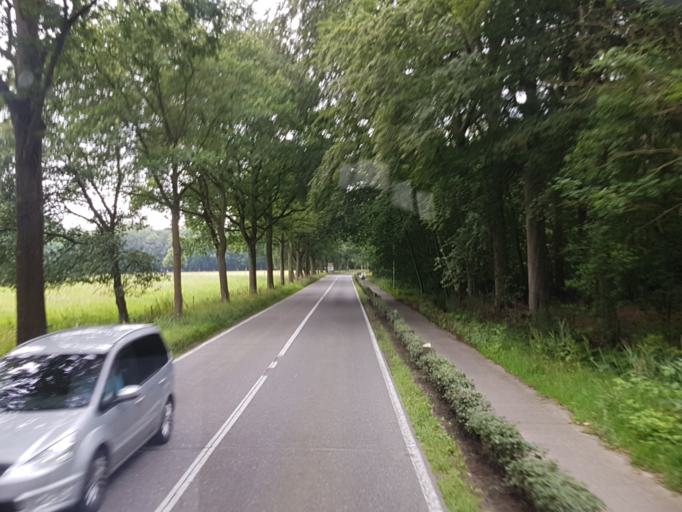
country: BE
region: Flanders
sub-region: Provincie Antwerpen
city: Schilde
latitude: 51.2218
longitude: 4.5994
